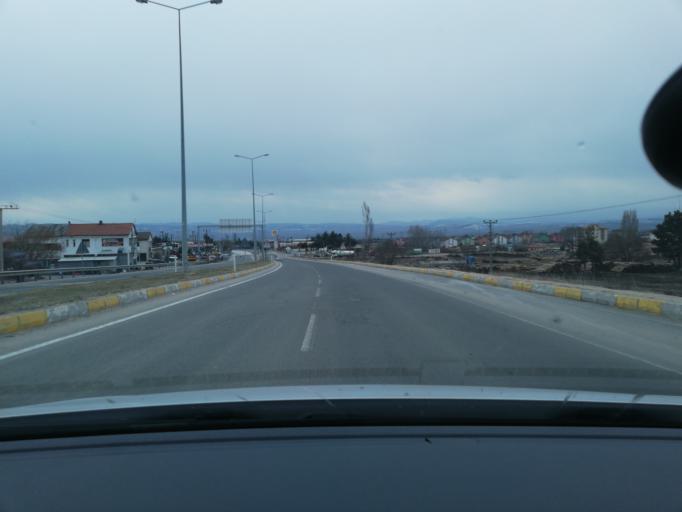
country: TR
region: Bolu
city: Gerede
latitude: 40.7904
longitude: 32.2083
